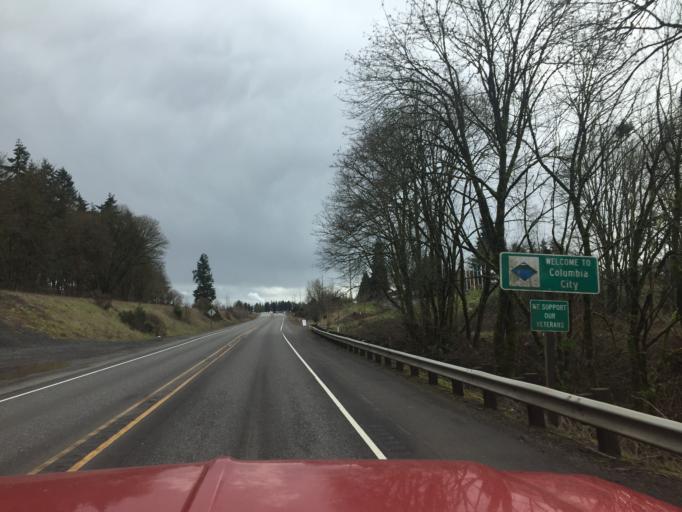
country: US
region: Oregon
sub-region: Columbia County
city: Columbia City
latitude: 45.9062
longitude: -122.8199
